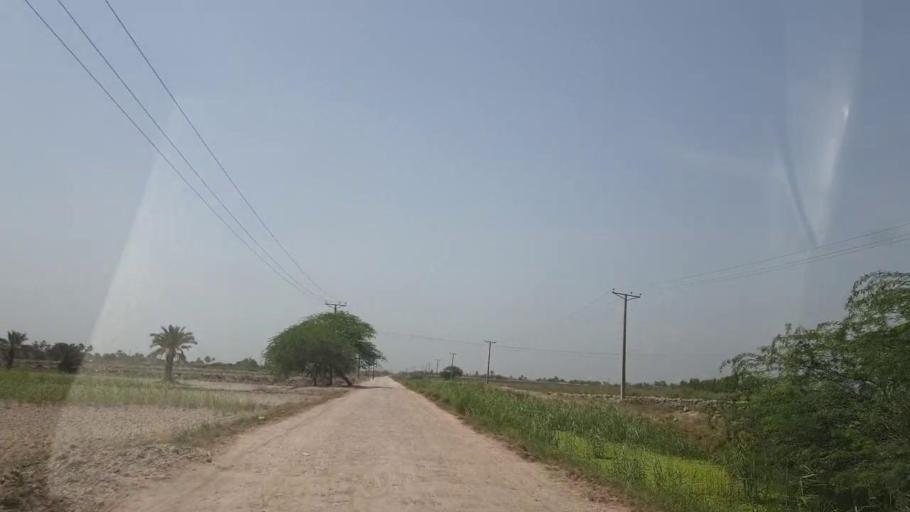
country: PK
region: Sindh
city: Ranipur
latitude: 27.3047
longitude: 68.5451
